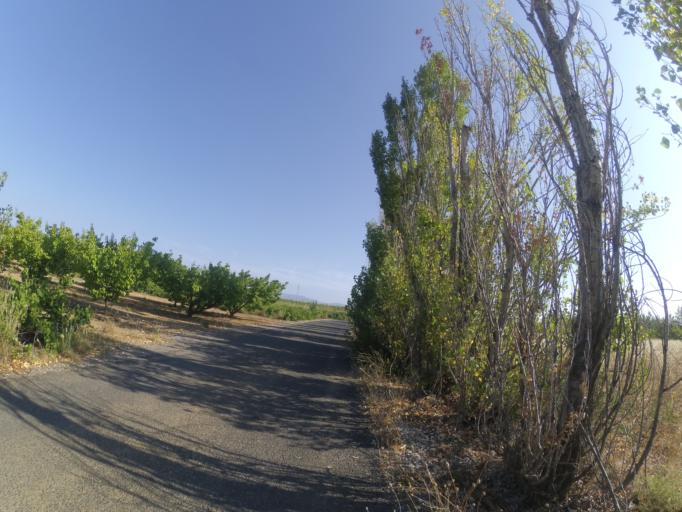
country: FR
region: Languedoc-Roussillon
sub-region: Departement des Pyrenees-Orientales
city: Peyrestortes
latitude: 42.7868
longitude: 2.8426
